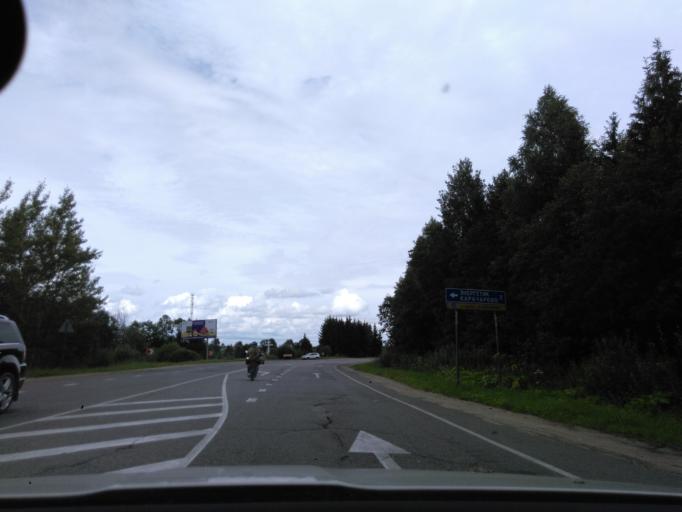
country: RU
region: Tverskaya
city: Konakovo
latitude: 56.6666
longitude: 36.7184
